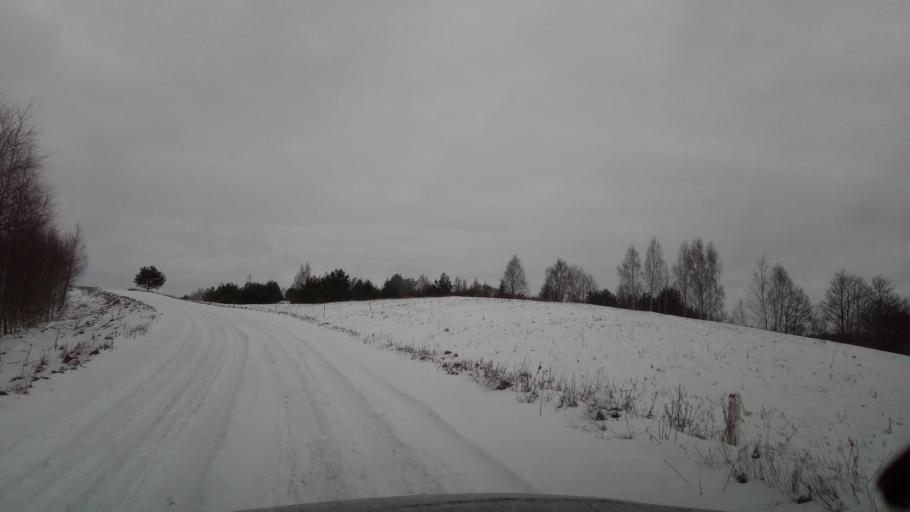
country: LT
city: Zarasai
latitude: 55.6836
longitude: 26.1060
